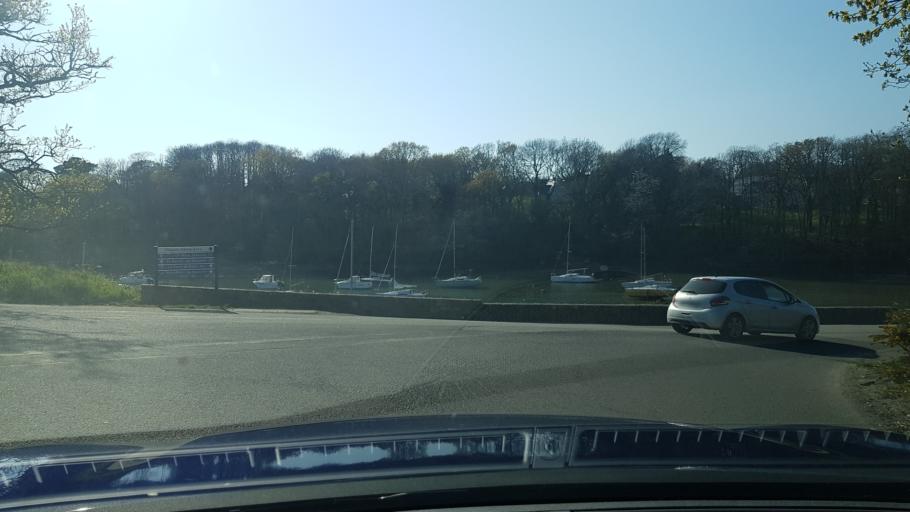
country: FR
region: Brittany
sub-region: Departement du Finistere
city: Clohars-Carnoet
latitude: 47.7766
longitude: -3.6035
